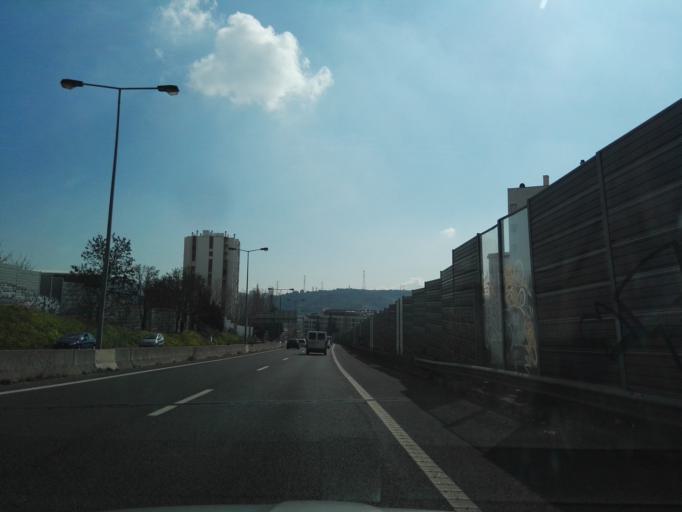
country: PT
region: Lisbon
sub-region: Odivelas
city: Povoa de Santo Adriao
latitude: 38.7963
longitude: -9.1741
